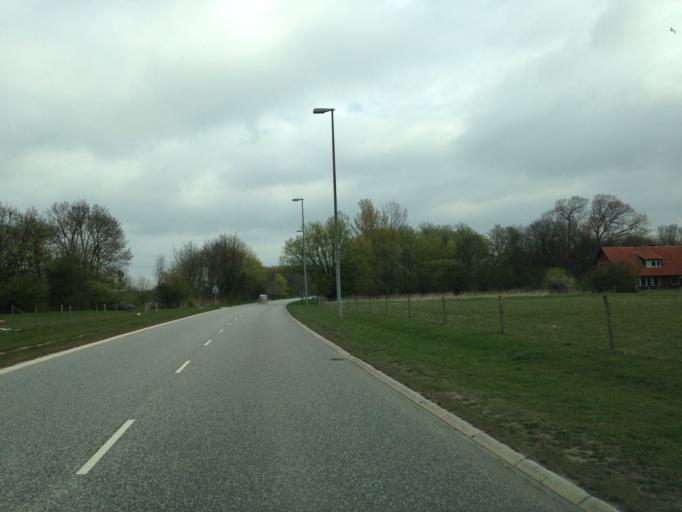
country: DK
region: Capital Region
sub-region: Ishoj Kommune
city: Ishoj
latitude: 55.6066
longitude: 12.3271
